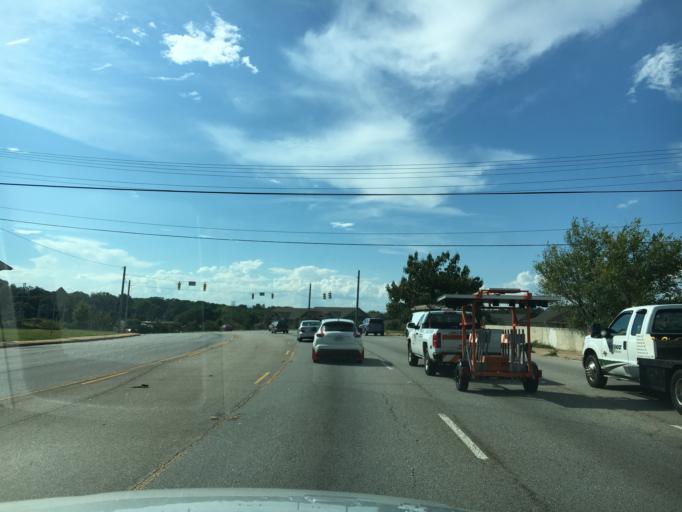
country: US
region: South Carolina
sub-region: Greenville County
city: Sans Souci
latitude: 34.8702
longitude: -82.4177
